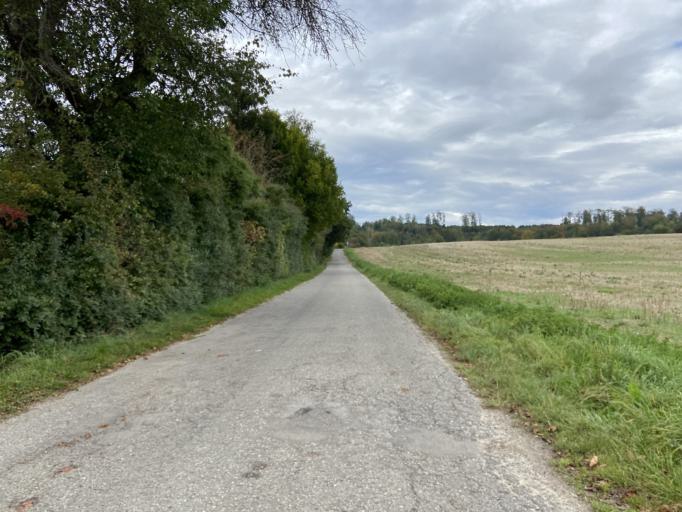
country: DE
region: Baden-Wuerttemberg
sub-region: Tuebingen Region
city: Sigmaringen
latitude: 48.0987
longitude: 9.2182
